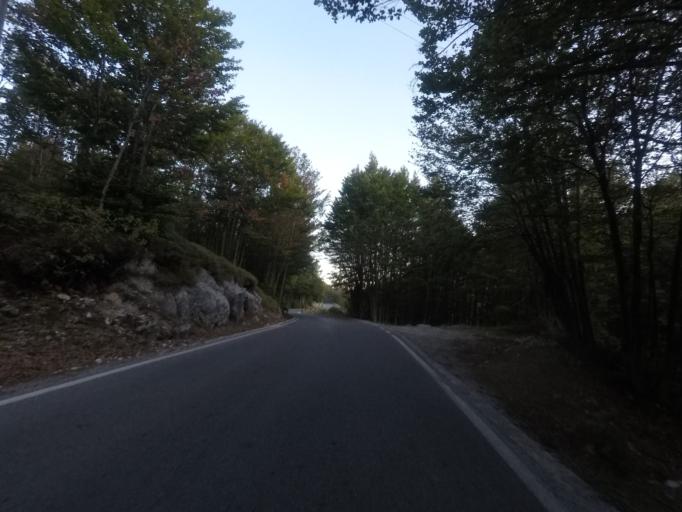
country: ME
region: Cetinje
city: Cetinje
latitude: 42.3729
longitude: 18.8698
